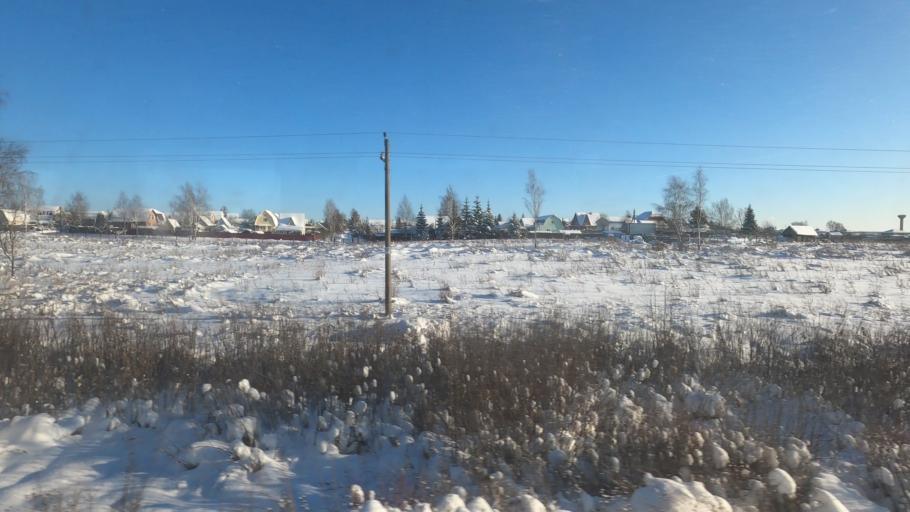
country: RU
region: Moskovskaya
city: Orud'yevo
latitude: 56.4044
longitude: 37.4942
